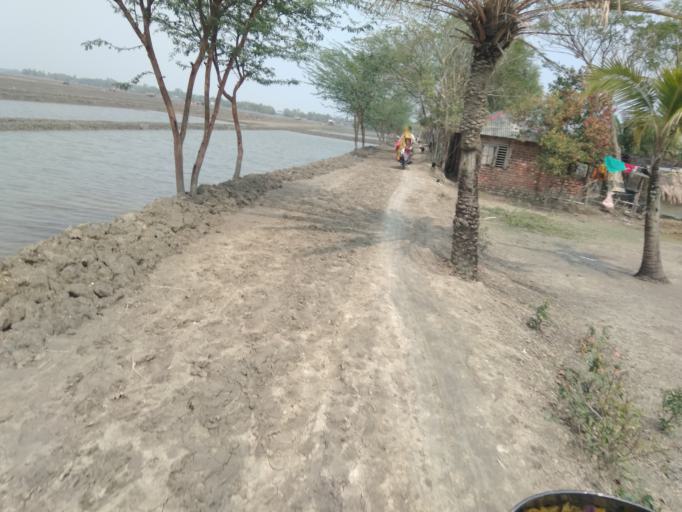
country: IN
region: West Bengal
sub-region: North 24 Parganas
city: Taki
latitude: 22.2754
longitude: 89.2842
